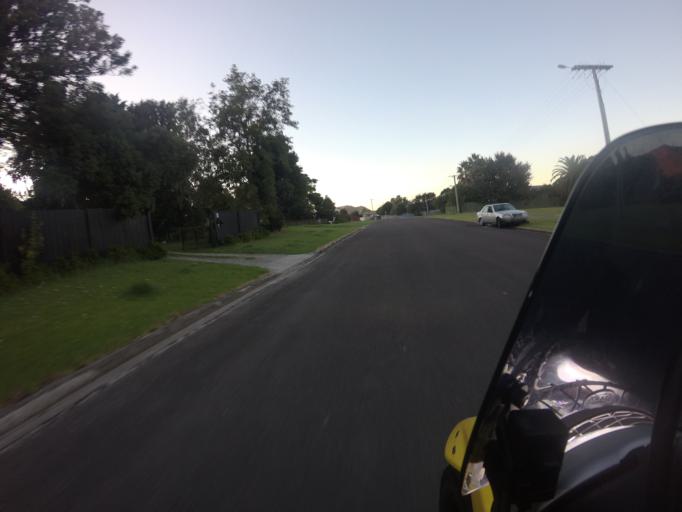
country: NZ
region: Gisborne
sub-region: Gisborne District
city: Gisborne
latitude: -38.6825
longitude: 178.0558
